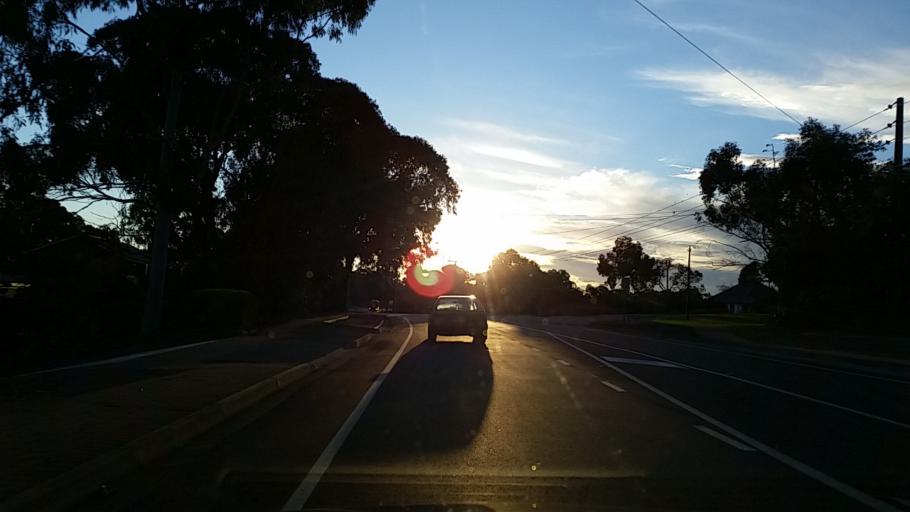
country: AU
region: South Australia
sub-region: Onkaparinga
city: Craigburn Farm
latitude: -35.0569
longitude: 138.6001
